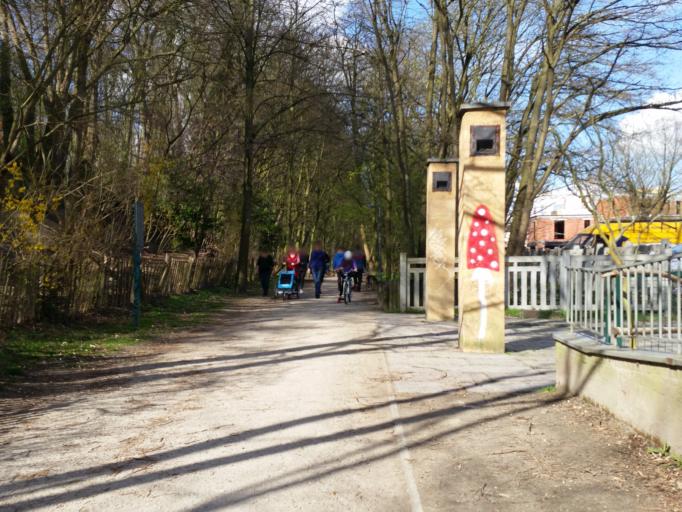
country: BE
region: Flanders
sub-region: Provincie Vlaams-Brabant
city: Kraainem
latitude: 50.8211
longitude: 4.4275
